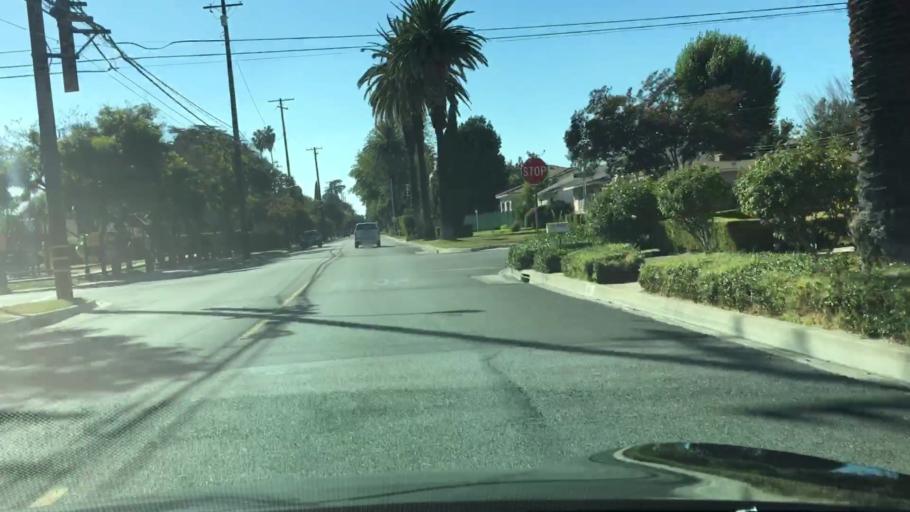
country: US
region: California
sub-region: Los Angeles County
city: Mayflower Village
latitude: 34.1144
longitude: -118.0182
